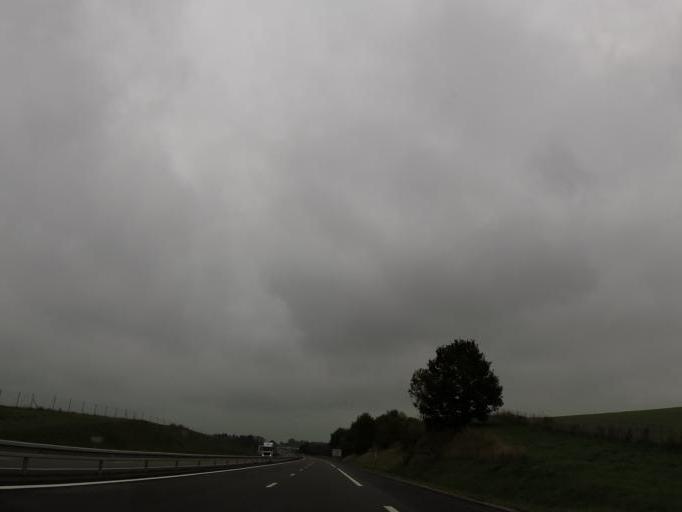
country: FR
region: Champagne-Ardenne
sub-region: Departement de la Marne
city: Sainte-Menehould
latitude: 49.0738
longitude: 4.8638
